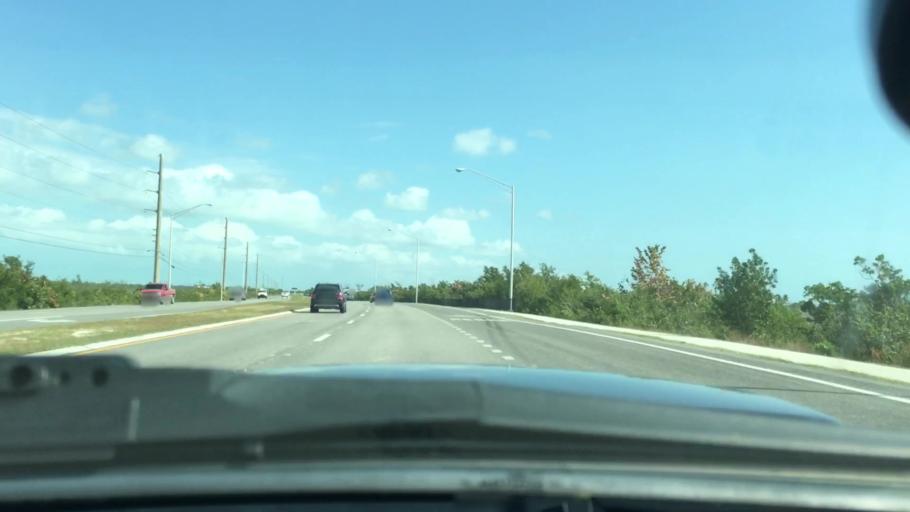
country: US
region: Florida
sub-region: Monroe County
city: Stock Island
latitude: 24.5797
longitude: -81.7073
